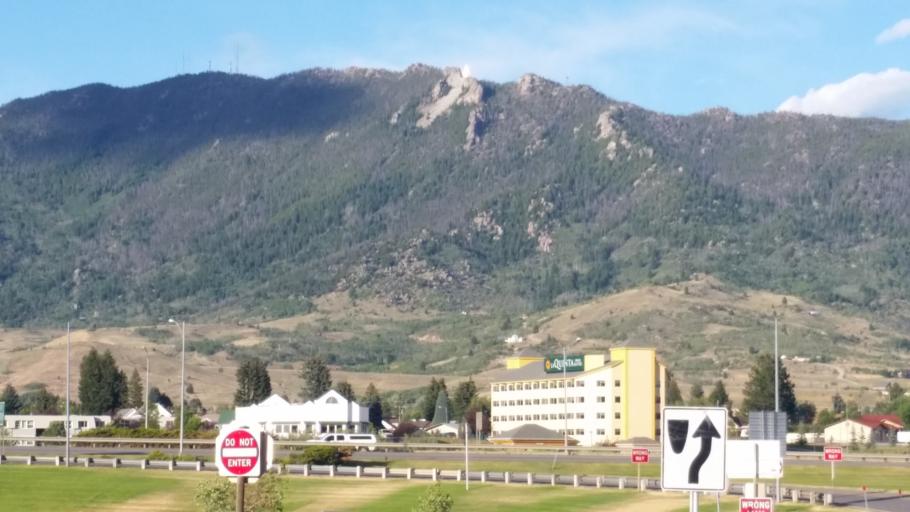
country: US
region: Montana
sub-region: Silver Bow County
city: Butte
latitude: 45.9823
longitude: -112.5086
